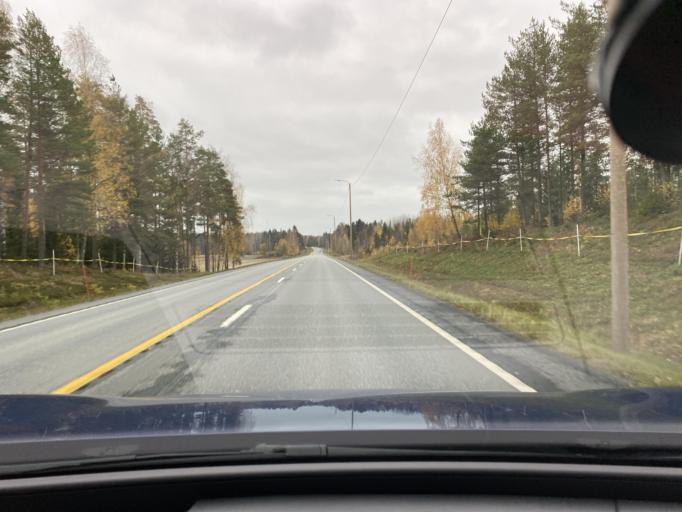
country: FI
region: Varsinais-Suomi
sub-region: Vakka-Suomi
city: Laitila
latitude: 60.9432
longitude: 21.6014
